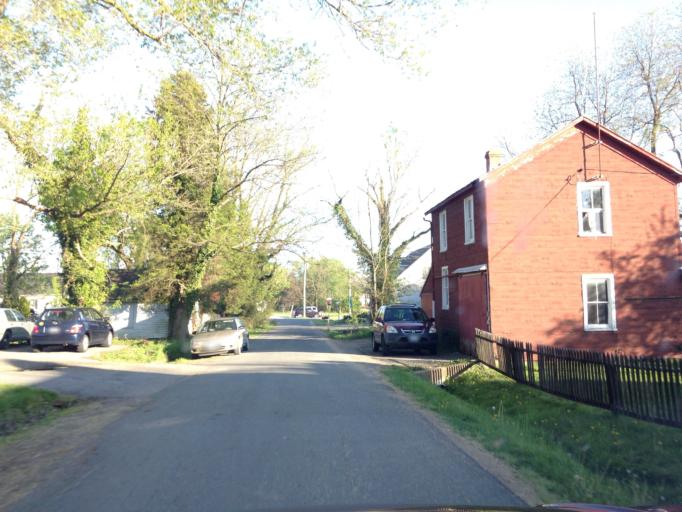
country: US
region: Virginia
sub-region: Loudoun County
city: Lovettsville
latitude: 39.2722
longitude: -77.6370
